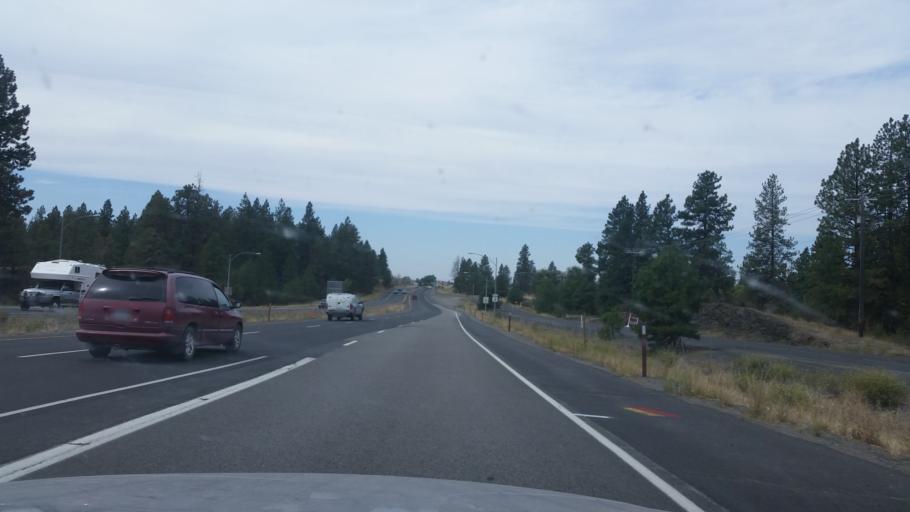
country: US
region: Washington
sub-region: Spokane County
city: Spokane
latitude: 47.6433
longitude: -117.5045
